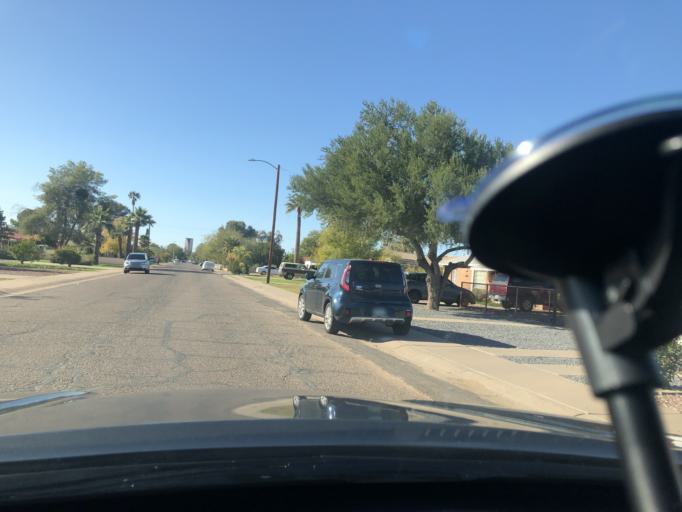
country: US
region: Arizona
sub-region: Maricopa County
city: Phoenix
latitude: 33.4685
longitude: -112.0441
